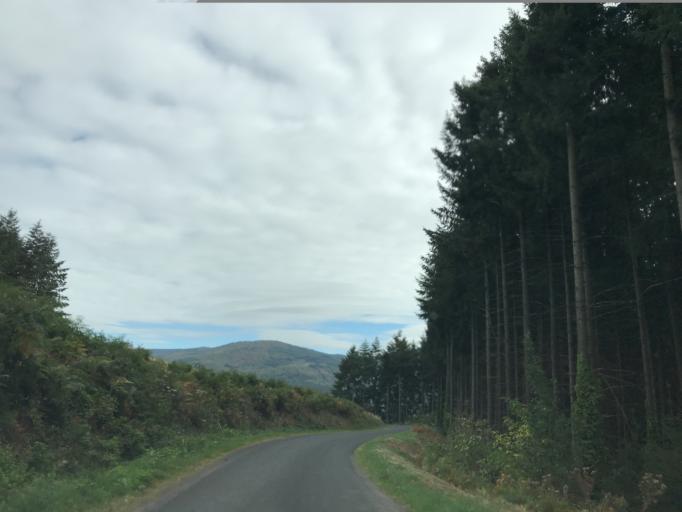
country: FR
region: Auvergne
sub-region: Departement du Puy-de-Dome
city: Escoutoux
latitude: 45.8226
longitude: 3.5890
